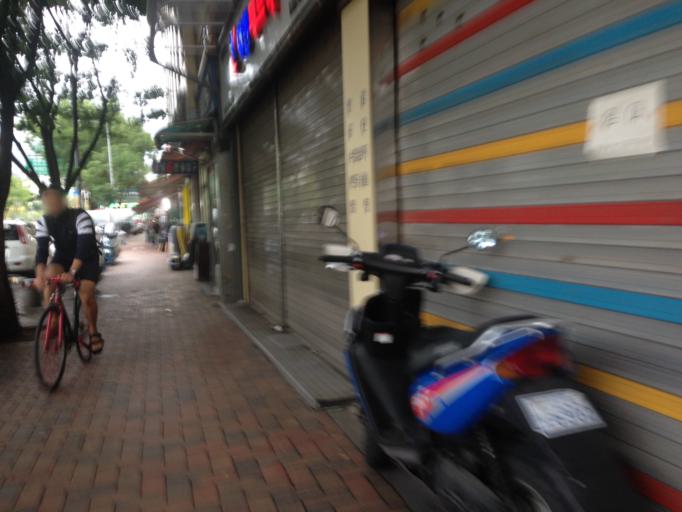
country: KR
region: Seoul
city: Seoul
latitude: 37.5693
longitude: 126.9990
